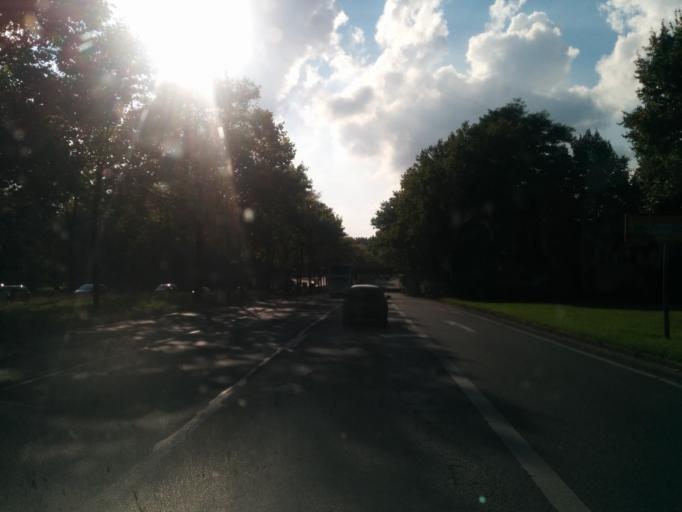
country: DE
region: North Rhine-Westphalia
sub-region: Regierungsbezirk Arnsberg
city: Dortmund
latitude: 51.4991
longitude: 7.4711
